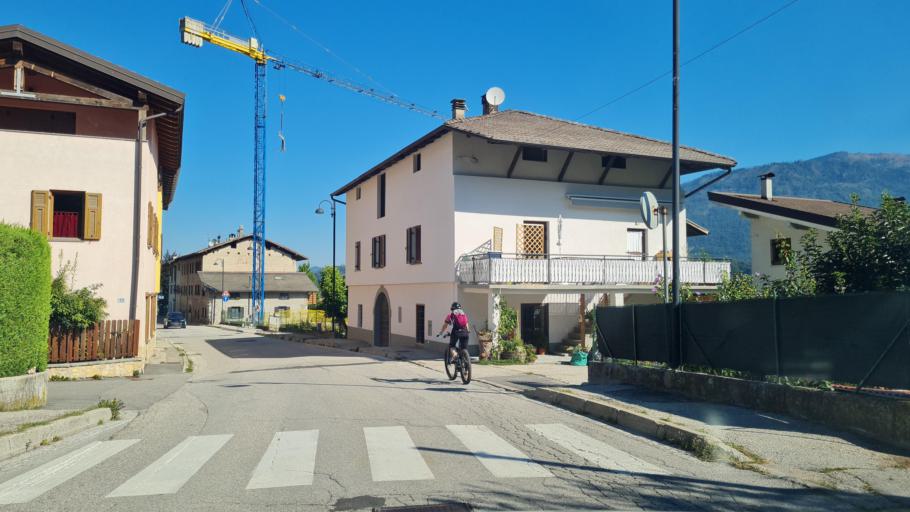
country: IT
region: Trentino-Alto Adige
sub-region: Provincia di Trento
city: Caldonazzo
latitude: 45.9879
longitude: 11.2662
